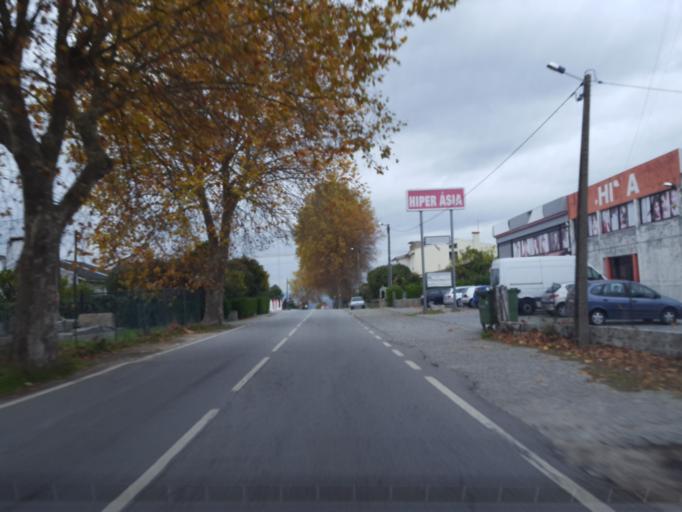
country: PT
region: Porto
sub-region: Marco de Canaveses
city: Marco de Canavezes
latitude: 41.1720
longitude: -8.1513
